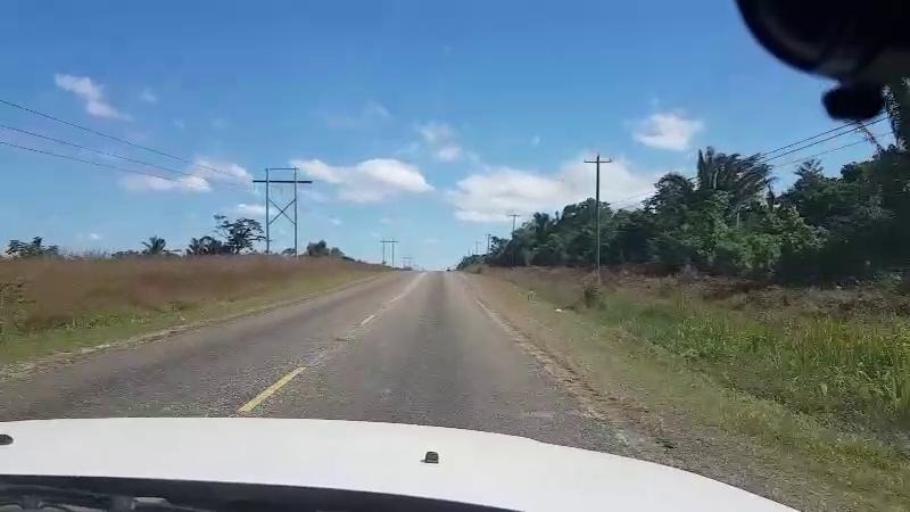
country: BZ
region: Cayo
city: Belmopan
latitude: 17.2768
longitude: -88.7336
